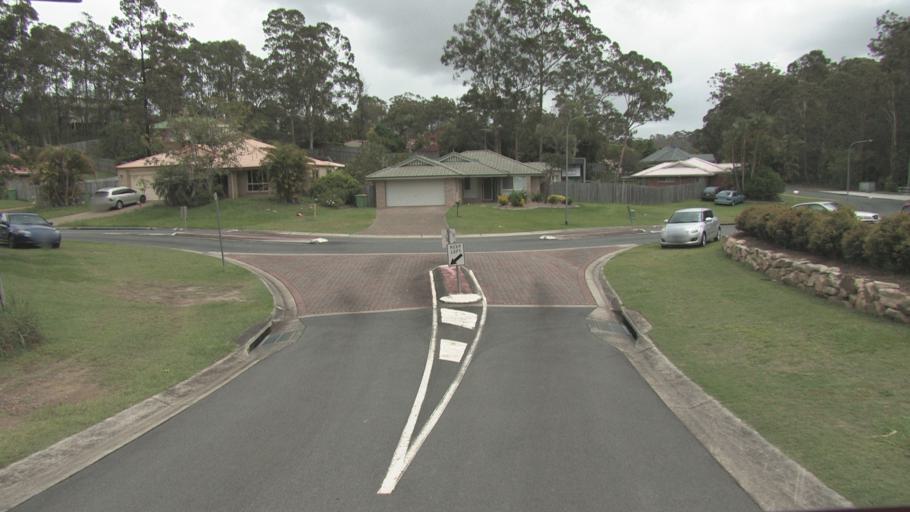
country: AU
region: Queensland
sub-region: Logan
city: Slacks Creek
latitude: -27.6420
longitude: 153.1927
